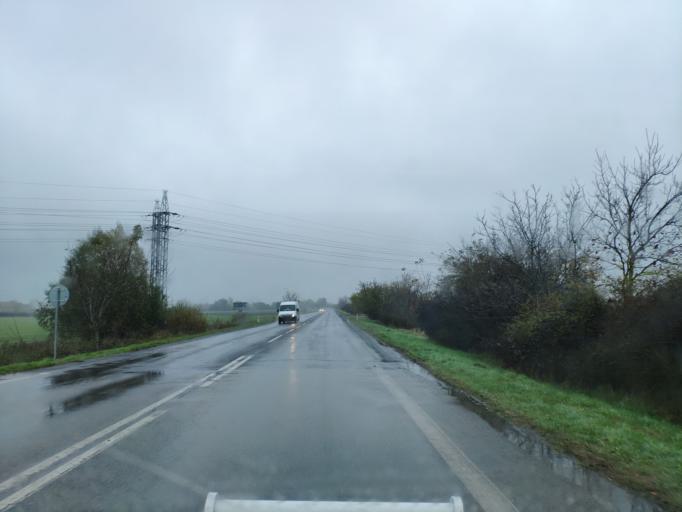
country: SK
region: Kosicky
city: Cierna nad Tisou
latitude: 48.4295
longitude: 21.9860
